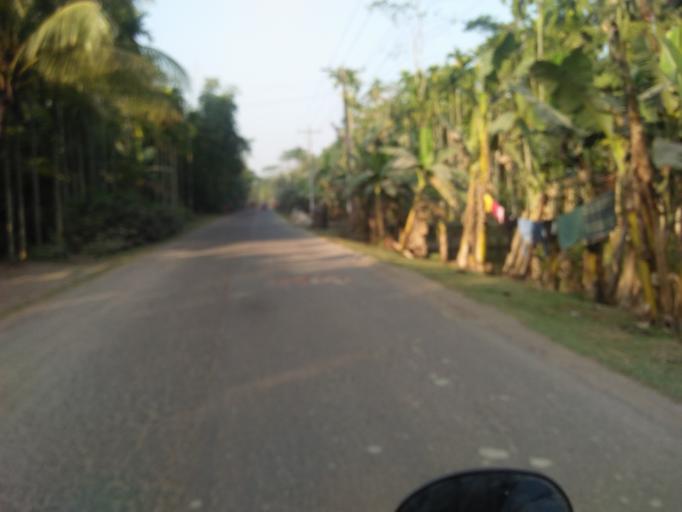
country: BD
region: Barisal
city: Bhola
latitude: 22.7432
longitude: 90.6343
